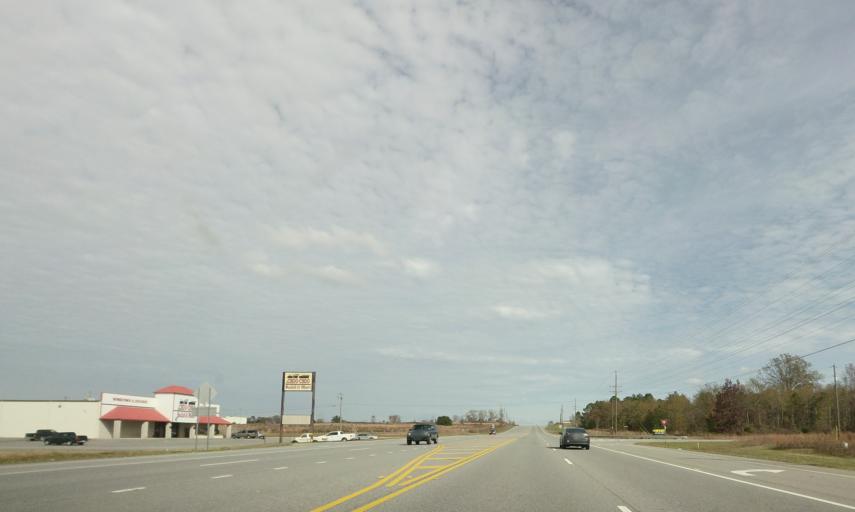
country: US
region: Georgia
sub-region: Laurens County
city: Dublin
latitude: 32.5048
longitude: -82.9700
